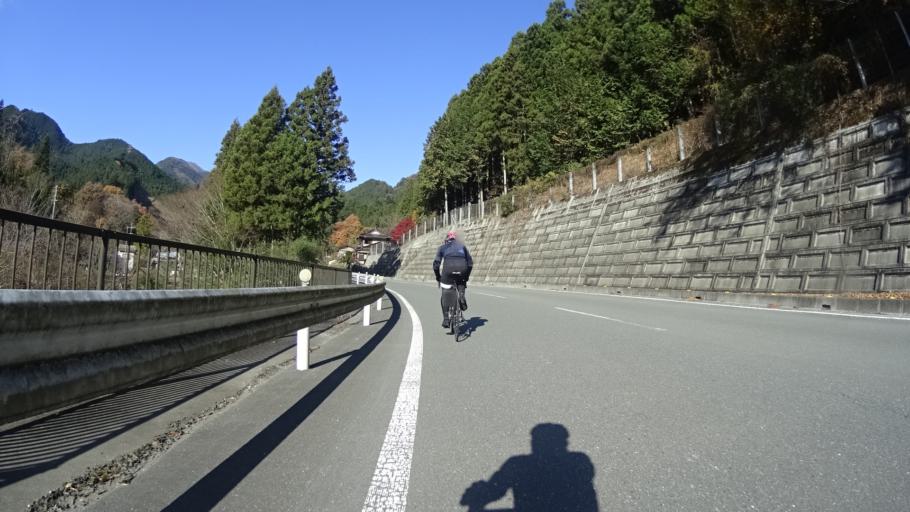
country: JP
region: Saitama
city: Chichibu
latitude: 35.9096
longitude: 139.1507
